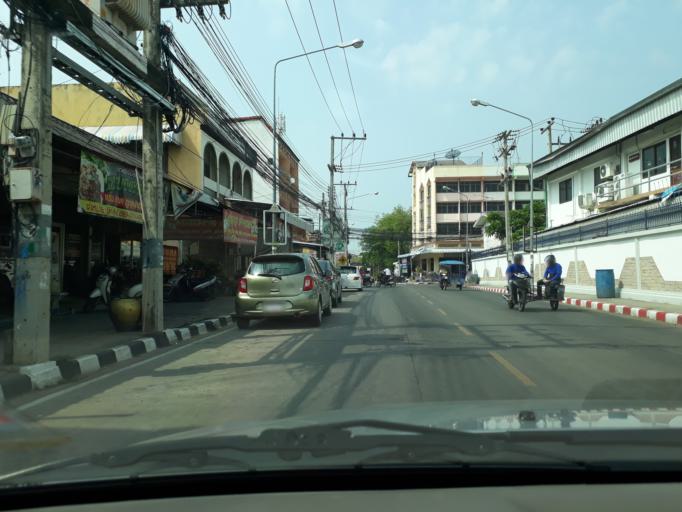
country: TH
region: Khon Kaen
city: Khon Kaen
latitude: 16.4267
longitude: 102.8369
